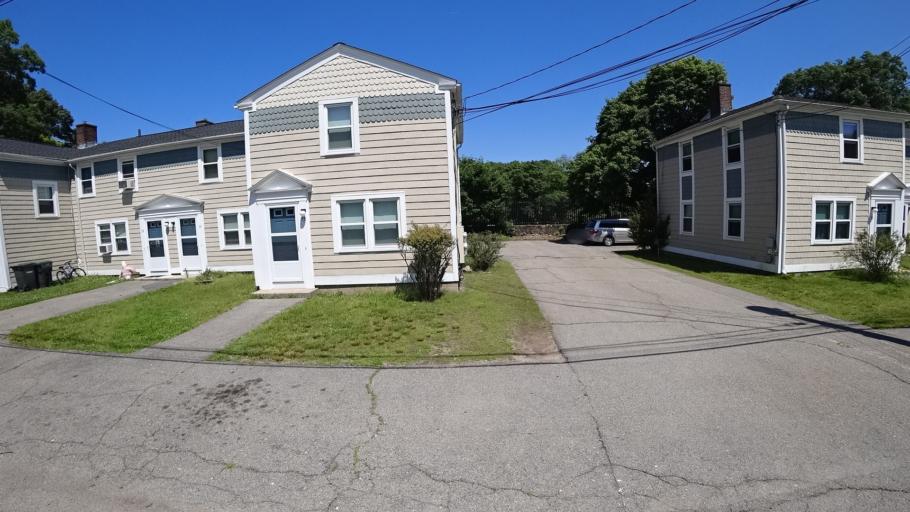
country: US
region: Massachusetts
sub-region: Norfolk County
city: Dedham
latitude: 42.2462
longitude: -71.1457
